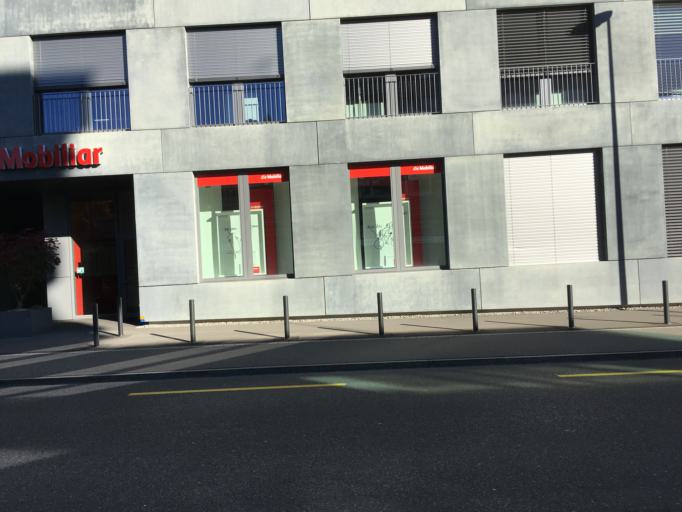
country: CH
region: Zurich
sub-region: Bezirk Hinwil
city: Wetzikon / Ober-Wetzikon
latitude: 47.3242
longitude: 8.7985
